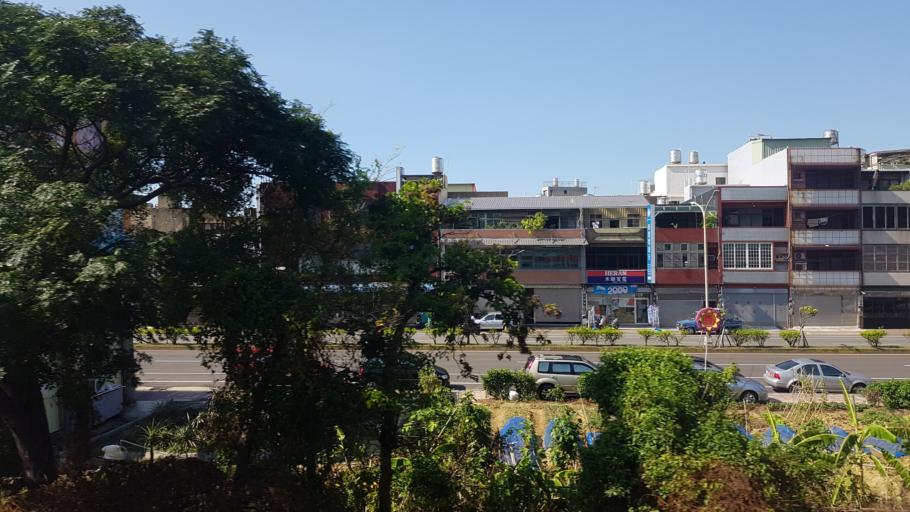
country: TW
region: Taiwan
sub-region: Hsinchu
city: Hsinchu
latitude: 24.7927
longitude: 120.9437
